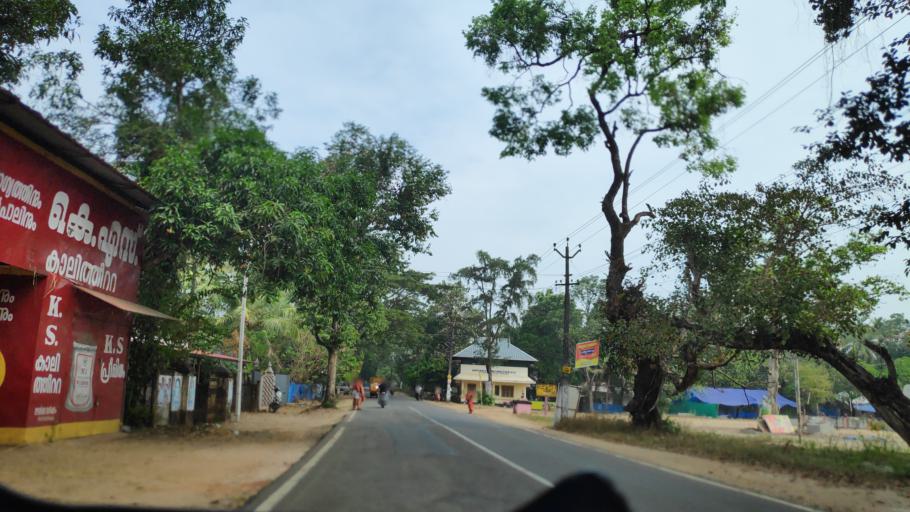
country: IN
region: Kerala
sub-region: Alappuzha
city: Vayalar
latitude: 9.7201
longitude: 76.3604
